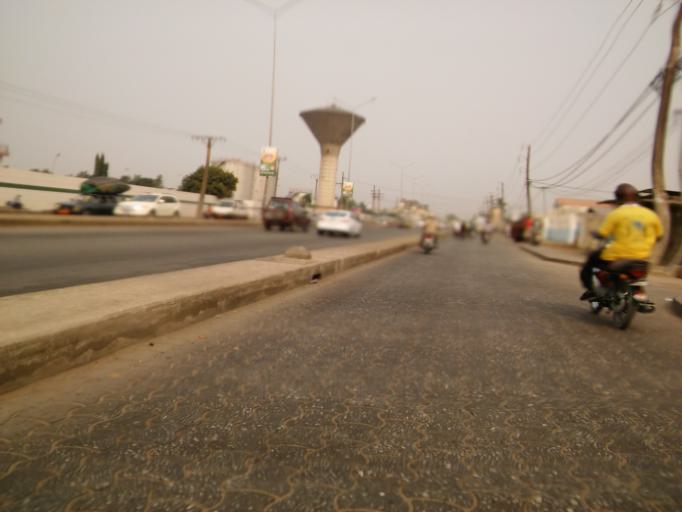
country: BJ
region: Littoral
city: Cotonou
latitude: 6.3772
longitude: 2.3861
